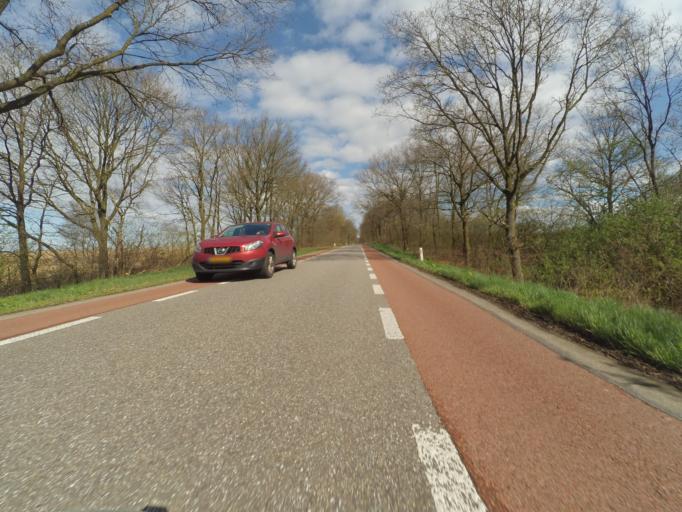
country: NL
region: Gelderland
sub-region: Gemeente Arnhem
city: Hoogkamp
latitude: 52.0897
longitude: 5.8791
